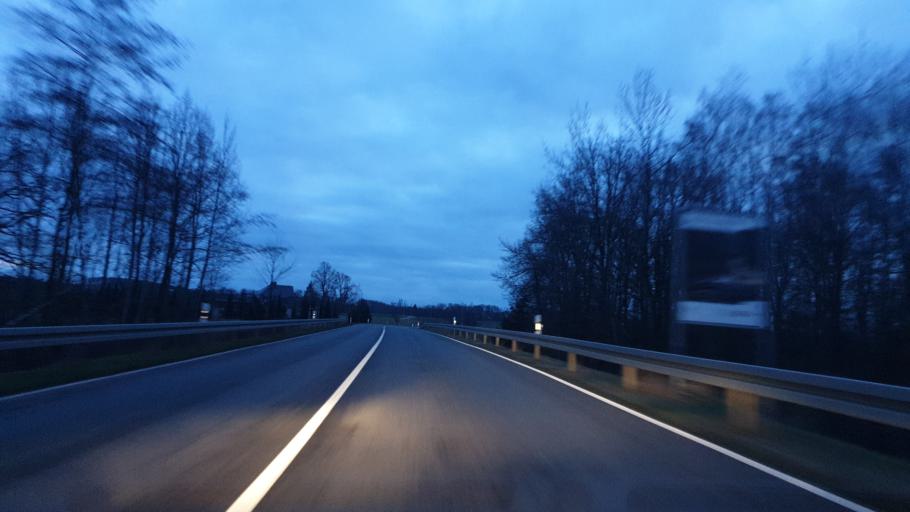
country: DE
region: Saxony
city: Lichtenstein
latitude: 50.7548
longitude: 12.6022
